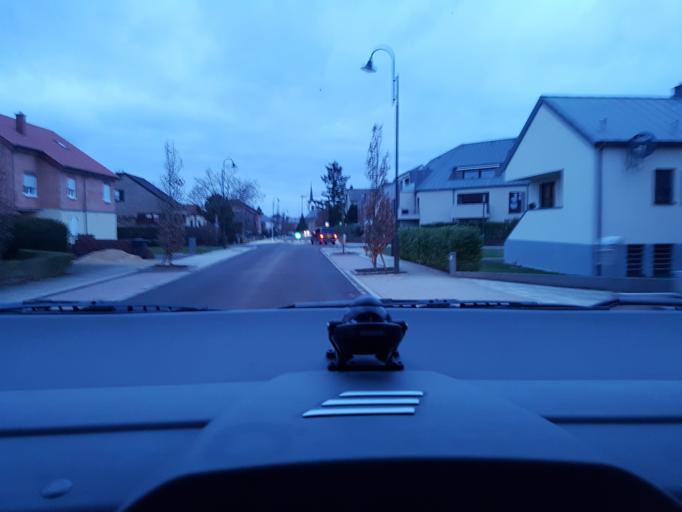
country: LU
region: Grevenmacher
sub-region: Canton de Remich
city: Mondorf-les-Bains
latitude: 49.5037
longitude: 6.3192
